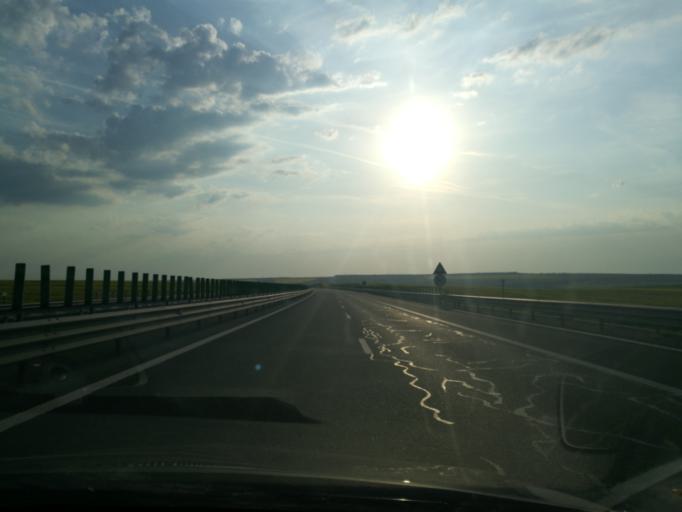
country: RO
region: Constanta
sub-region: Comuna Valu lui Traian
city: Valu lui Traian
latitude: 44.1406
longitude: 28.4582
